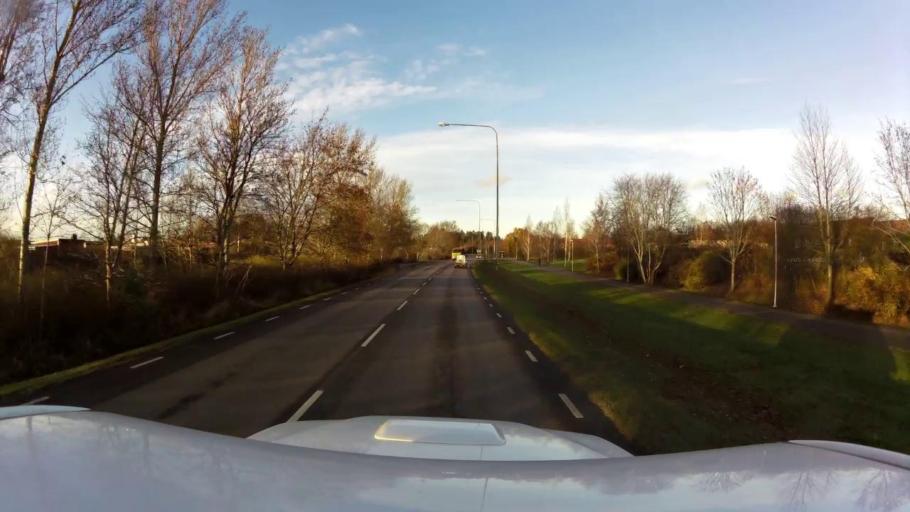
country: SE
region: OEstergoetland
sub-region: Linkopings Kommun
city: Linkoping
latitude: 58.3807
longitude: 15.6600
